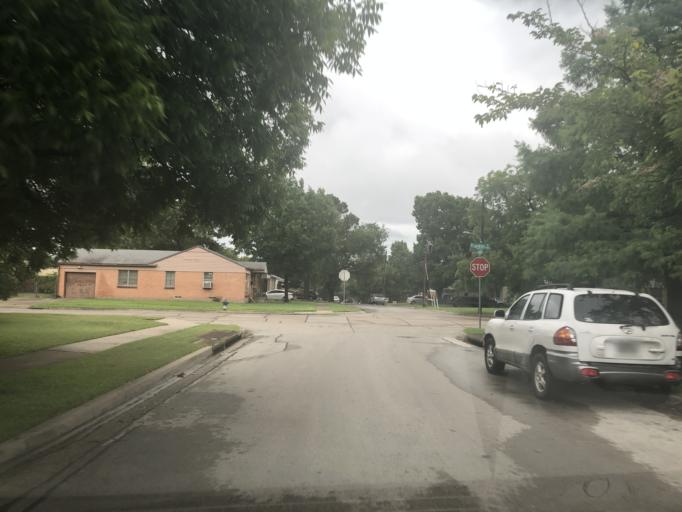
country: US
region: Texas
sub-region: Dallas County
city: Irving
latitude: 32.7999
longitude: -96.9500
